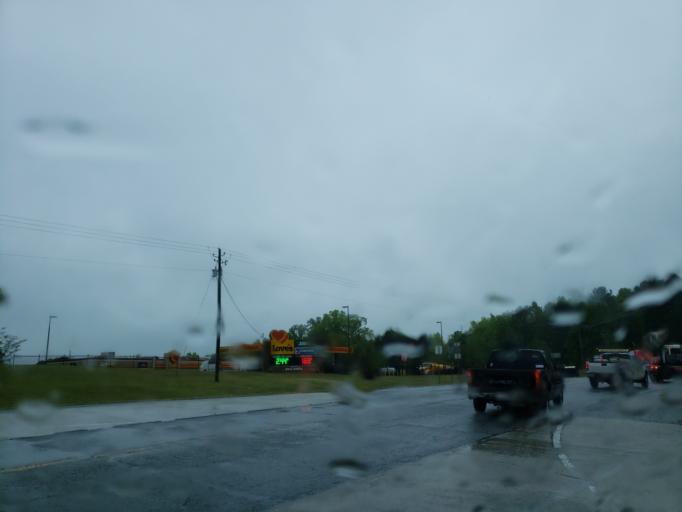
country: US
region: Georgia
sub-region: Haralson County
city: Bremen
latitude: 33.6906
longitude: -85.1885
